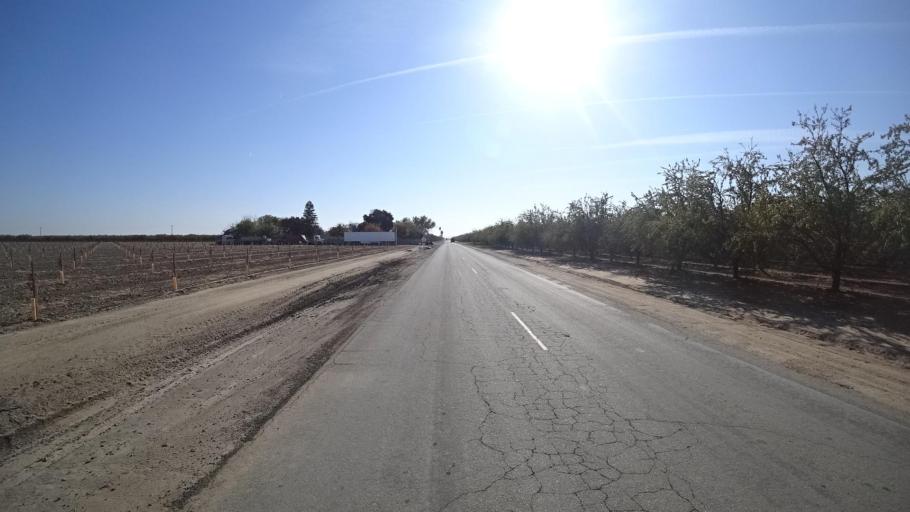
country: US
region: California
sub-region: Kern County
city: Wasco
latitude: 35.6541
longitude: -119.3487
